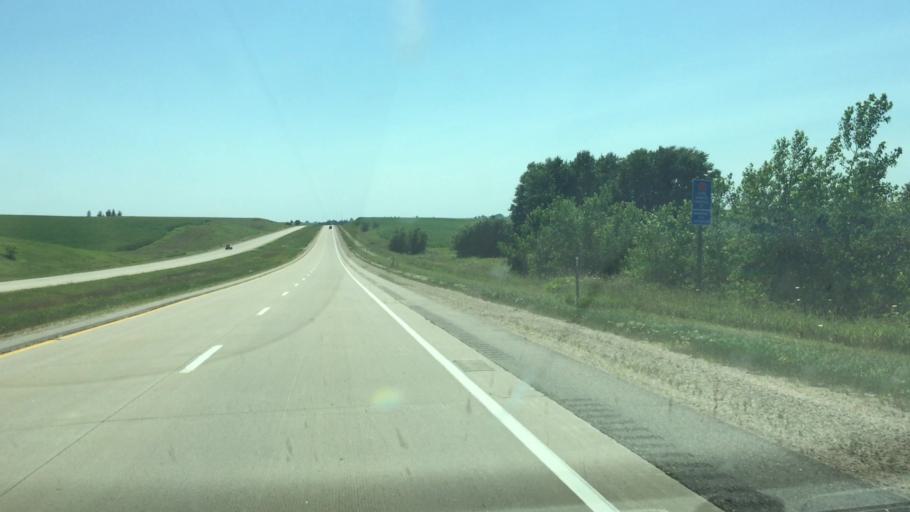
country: US
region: Iowa
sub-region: Dubuque County
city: Peosta
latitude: 42.3605
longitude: -90.8087
